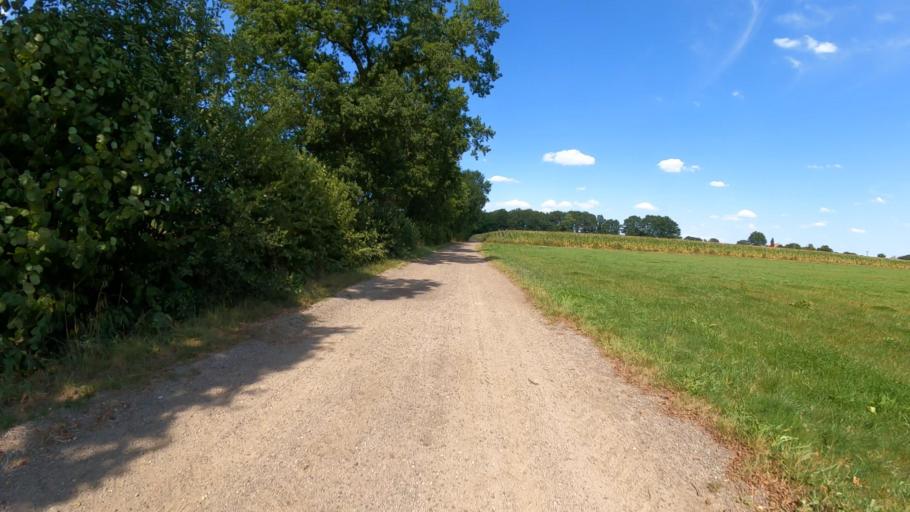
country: DE
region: Schleswig-Holstein
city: Ellerhoop
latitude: 53.7324
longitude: 9.7660
